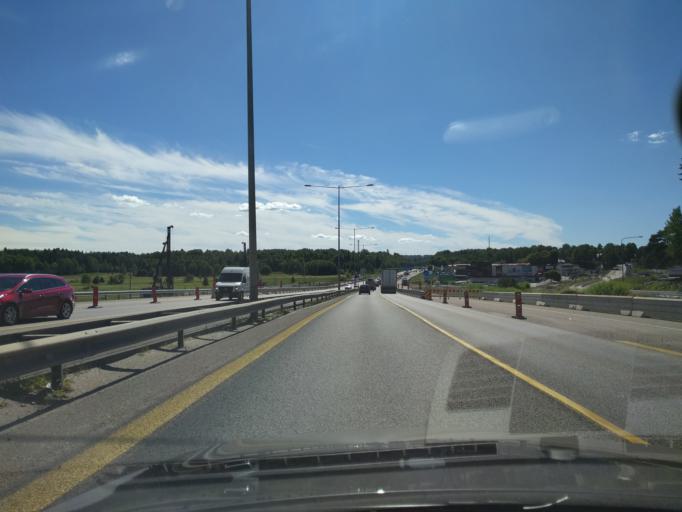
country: SE
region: Stockholm
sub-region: Haninge Kommun
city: Haninge
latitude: 59.1894
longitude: 18.1454
